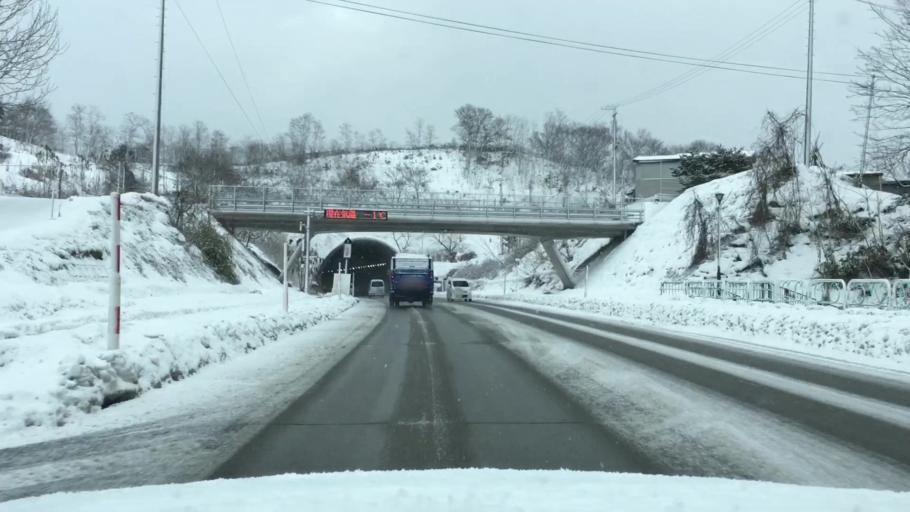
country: JP
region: Aomori
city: Hirosaki
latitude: 40.5252
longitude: 140.5611
